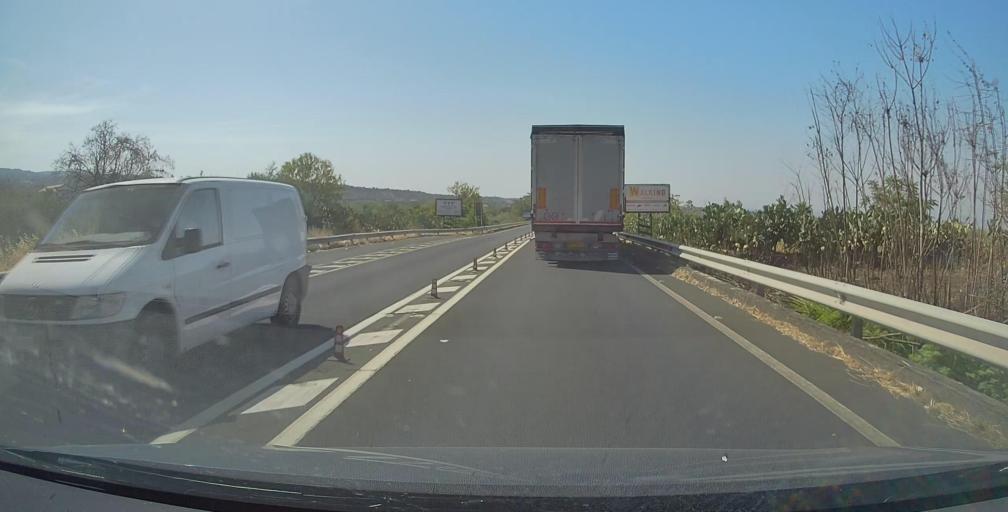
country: IT
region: Sicily
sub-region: Catania
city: Biancavilla
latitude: 37.6449
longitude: 14.8838
